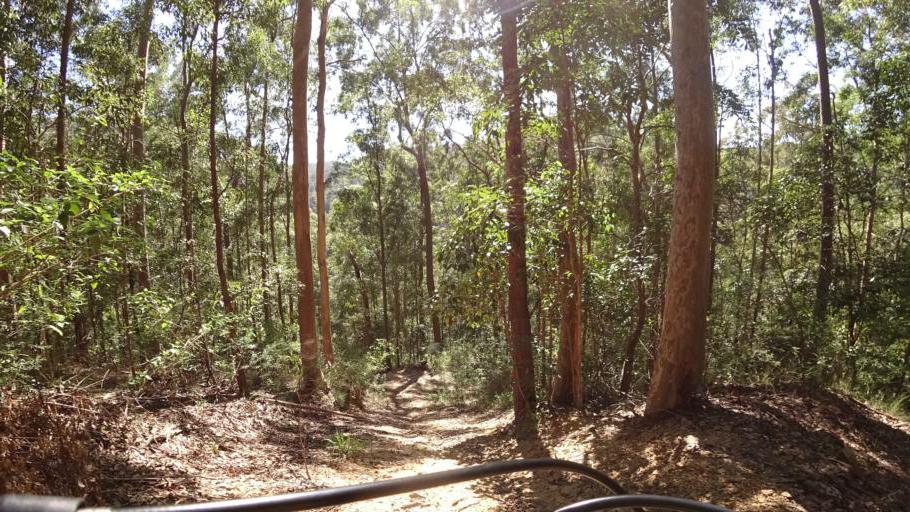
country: AU
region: Queensland
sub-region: Moreton Bay
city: Highvale
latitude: -27.4124
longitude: 152.7853
